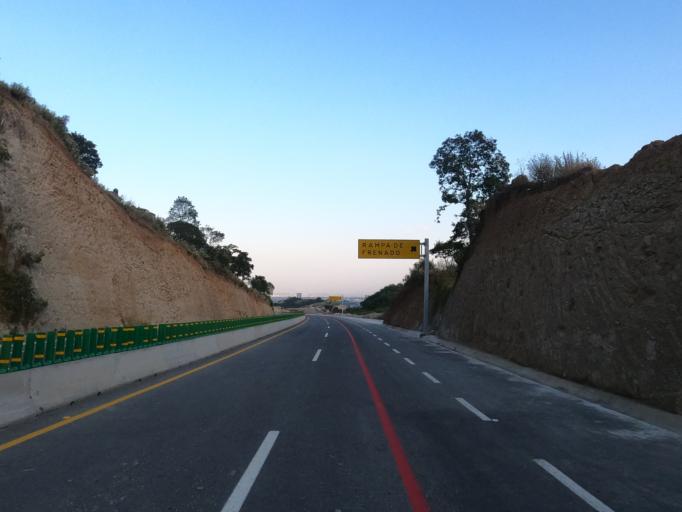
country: MX
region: Mexico
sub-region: Naucalpan de Juarez
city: Llano de las Flores (Barrio del Hueso)
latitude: 19.4227
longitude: -99.3261
